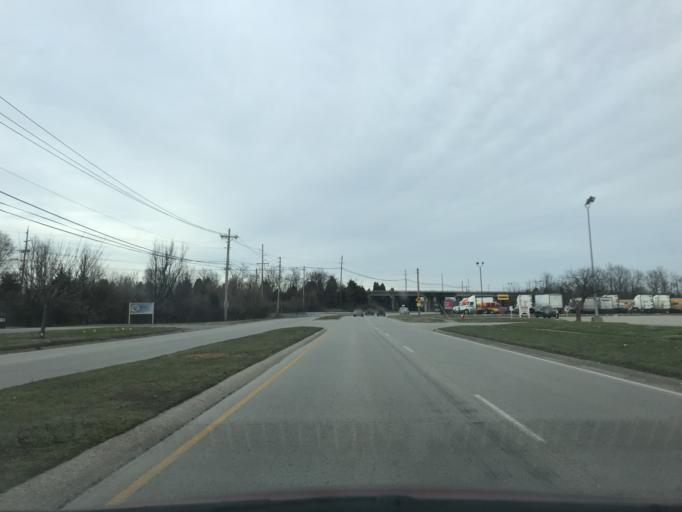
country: US
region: Kentucky
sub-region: Jefferson County
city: West Buechel
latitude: 38.1887
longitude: -85.6749
